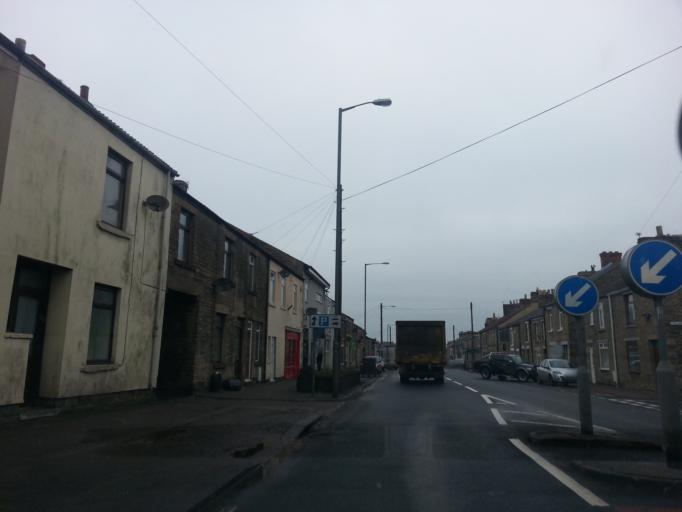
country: GB
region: England
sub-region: County Durham
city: Tow Law
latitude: 54.7425
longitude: -1.8140
